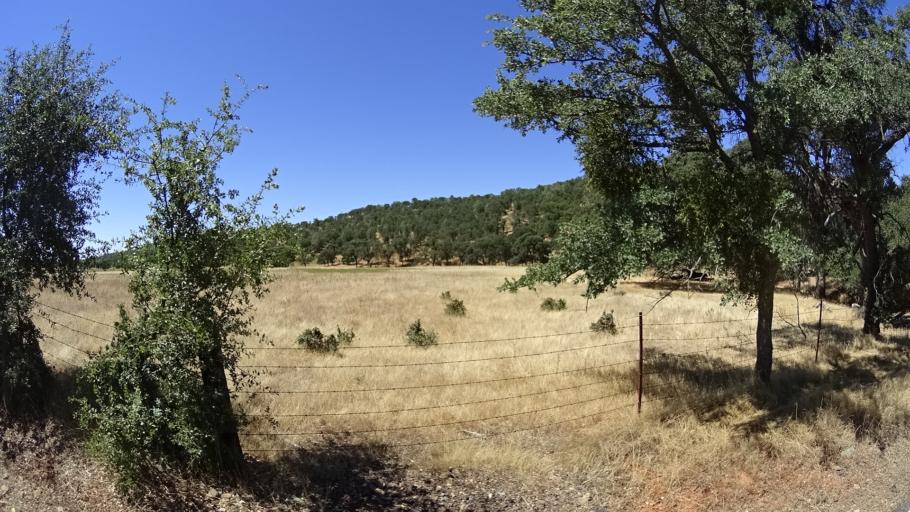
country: US
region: California
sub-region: Calaveras County
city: Copperopolis
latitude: 37.9963
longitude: -120.6557
